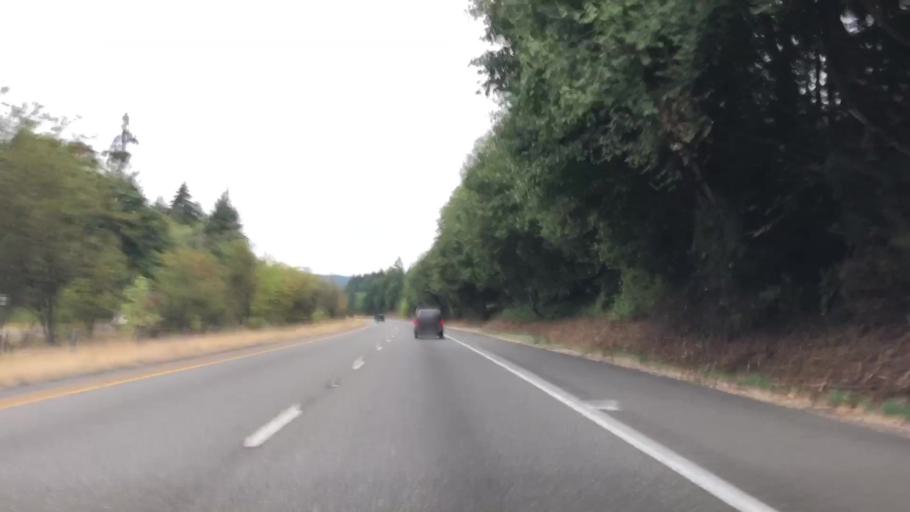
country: US
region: Washington
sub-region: Pierce County
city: Purdy
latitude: 47.3916
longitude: -122.6172
